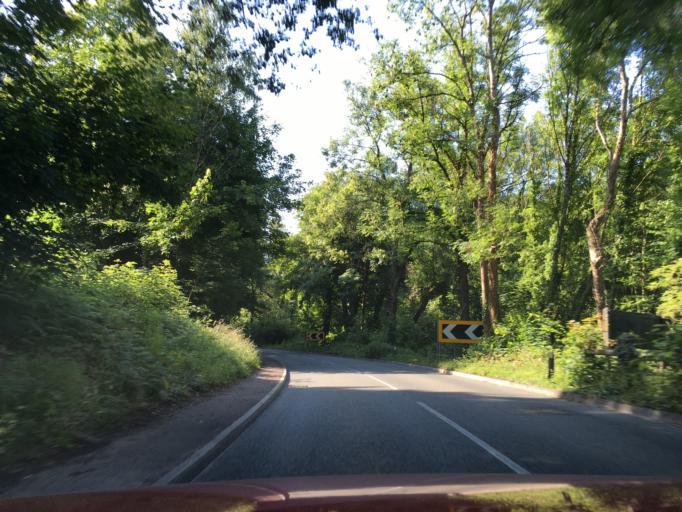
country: GB
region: England
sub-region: Gloucestershire
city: Lydney
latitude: 51.7340
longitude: -2.5376
